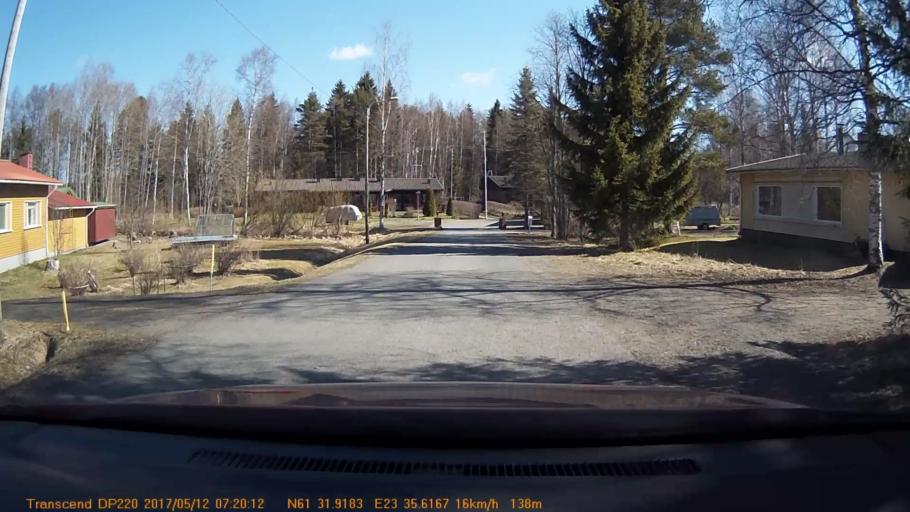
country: FI
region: Pirkanmaa
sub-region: Tampere
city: Yloejaervi
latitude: 61.5320
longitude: 23.5936
